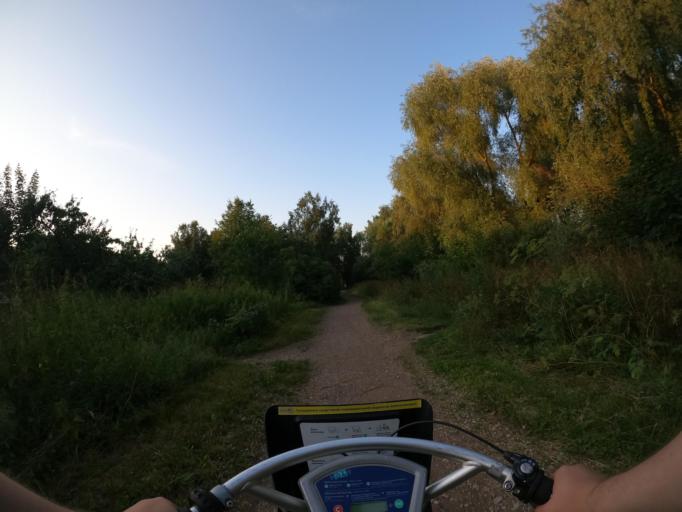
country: RU
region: Moscow
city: Strogino
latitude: 55.8091
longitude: 37.4197
